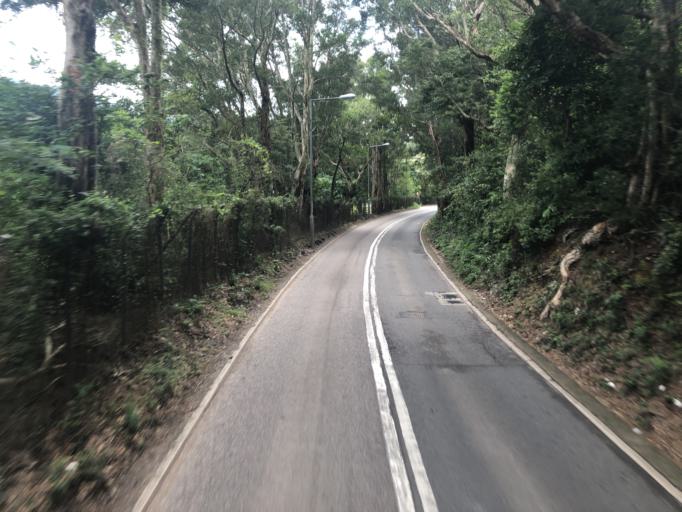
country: HK
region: Tai Po
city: Tai Po
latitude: 22.4874
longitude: 114.1165
